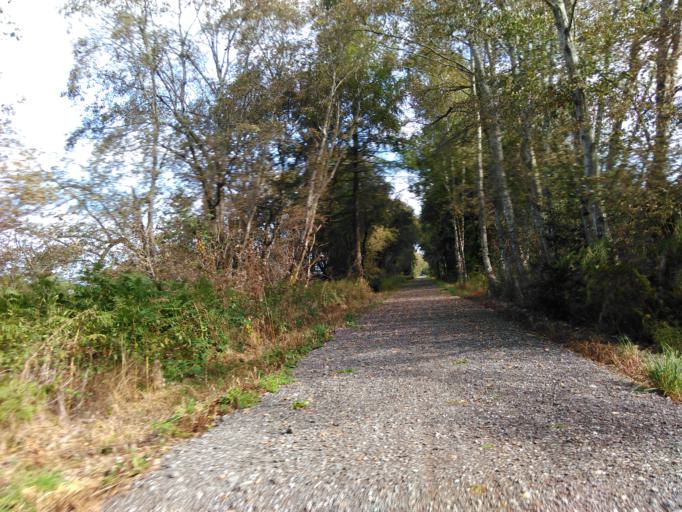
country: BE
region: Wallonia
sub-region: Province du Luxembourg
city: Vaux-sur-Sure
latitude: 49.9245
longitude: 5.5101
